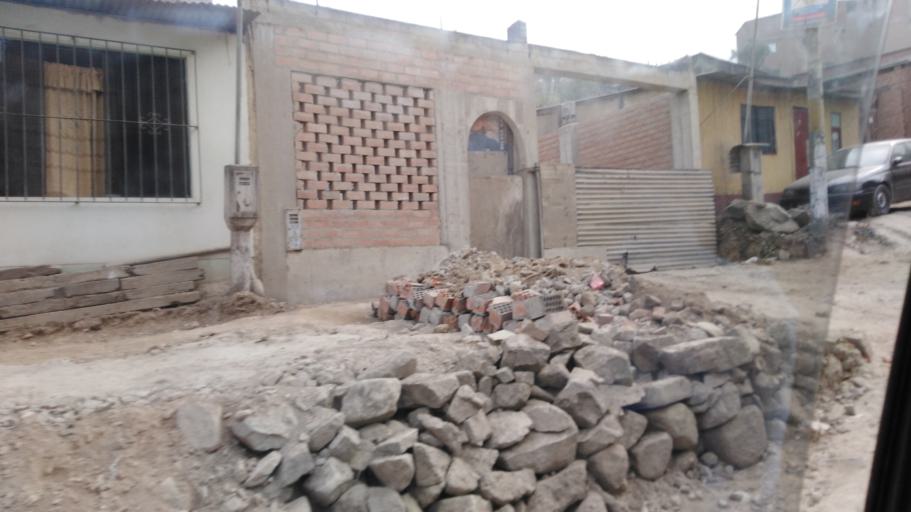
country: PE
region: Lima
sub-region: Lima
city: La Molina
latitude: -12.1468
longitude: -76.9286
